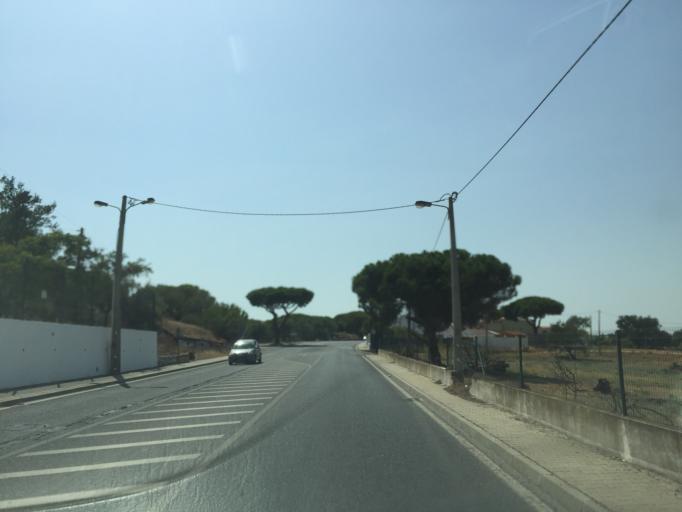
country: PT
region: Faro
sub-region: Albufeira
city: Ferreiras
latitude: 37.1088
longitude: -8.2037
